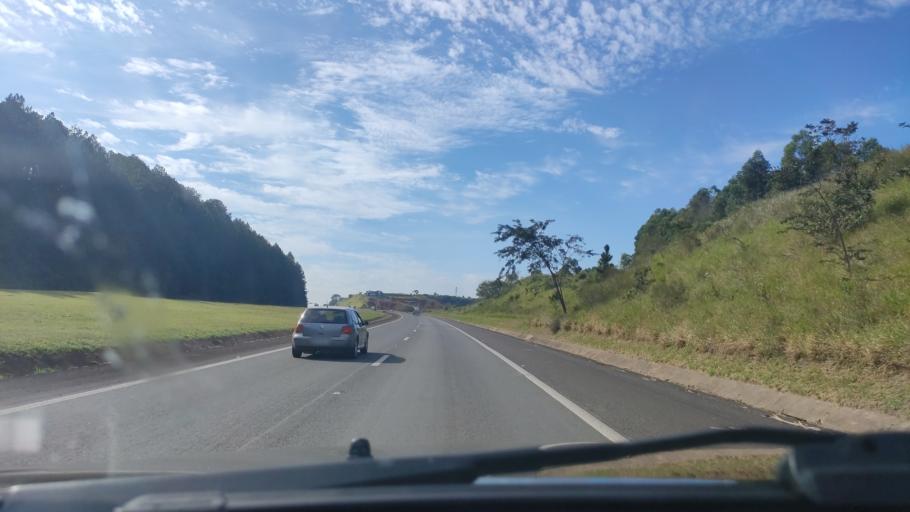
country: BR
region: Sao Paulo
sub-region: Itatinga
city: Itatinga
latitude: -23.1331
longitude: -48.4631
